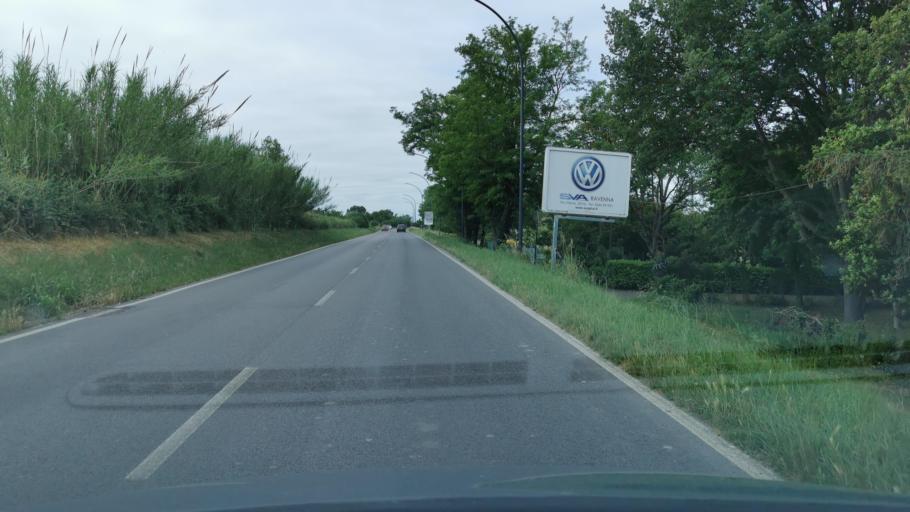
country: IT
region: Emilia-Romagna
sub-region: Provincia di Ravenna
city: Madonna Dell'Albero
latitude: 44.3918
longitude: 12.1970
